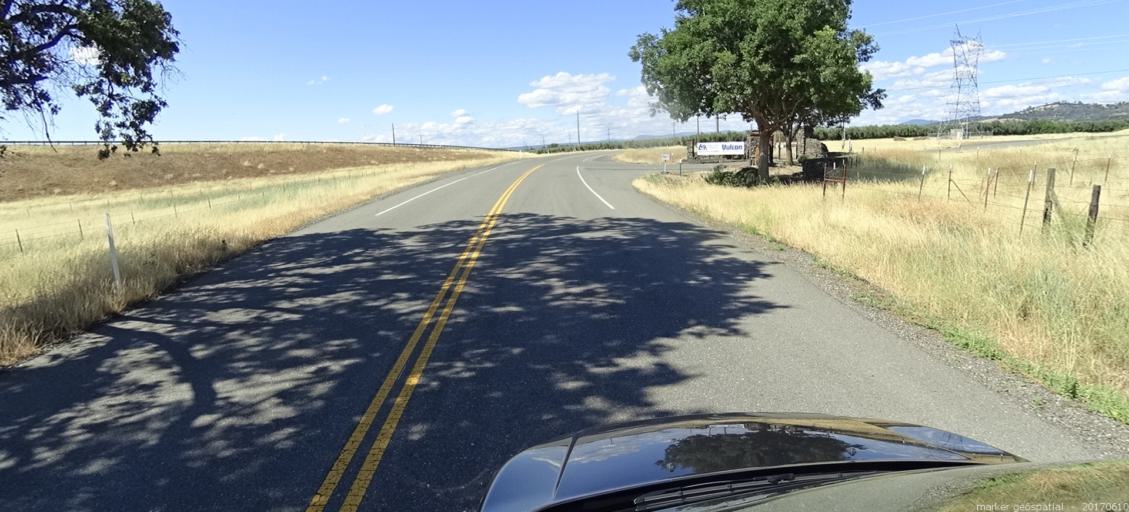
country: US
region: California
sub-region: Butte County
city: Thermalito
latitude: 39.5831
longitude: -121.6192
